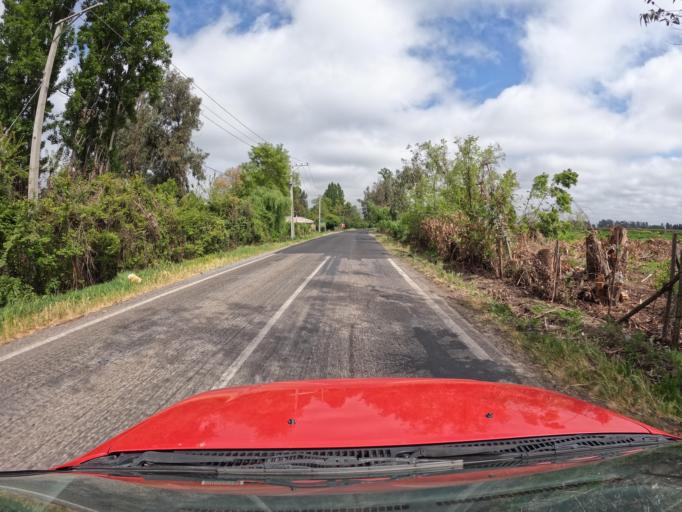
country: CL
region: O'Higgins
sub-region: Provincia de Colchagua
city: Santa Cruz
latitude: -34.6781
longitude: -71.3624
